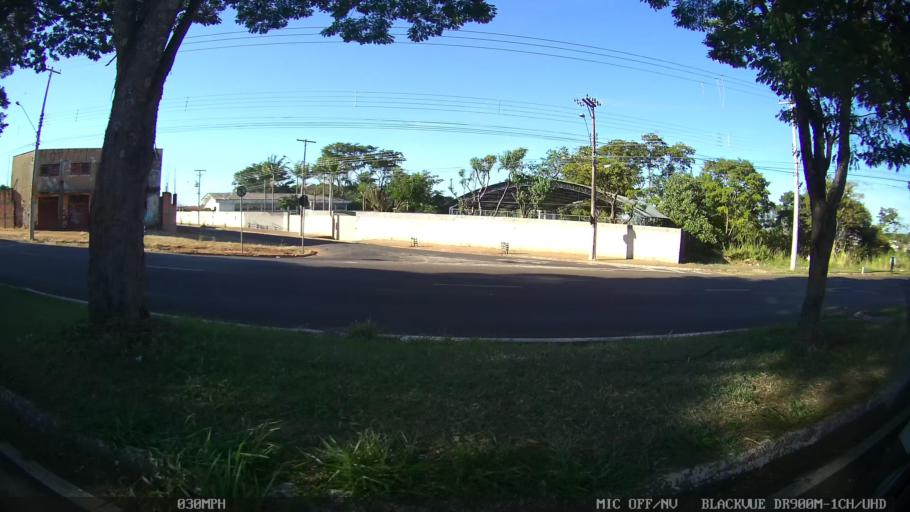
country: BR
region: Sao Paulo
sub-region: Franca
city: Franca
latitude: -20.5750
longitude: -47.3744
